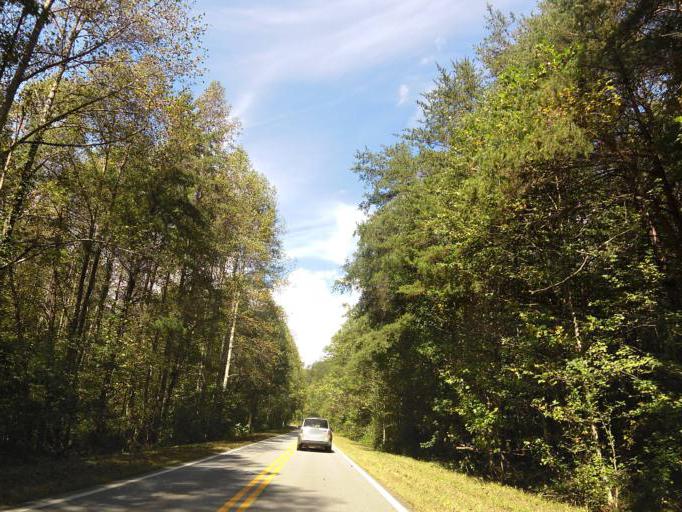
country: US
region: Georgia
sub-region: Pickens County
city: Jasper
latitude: 34.5108
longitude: -84.2783
